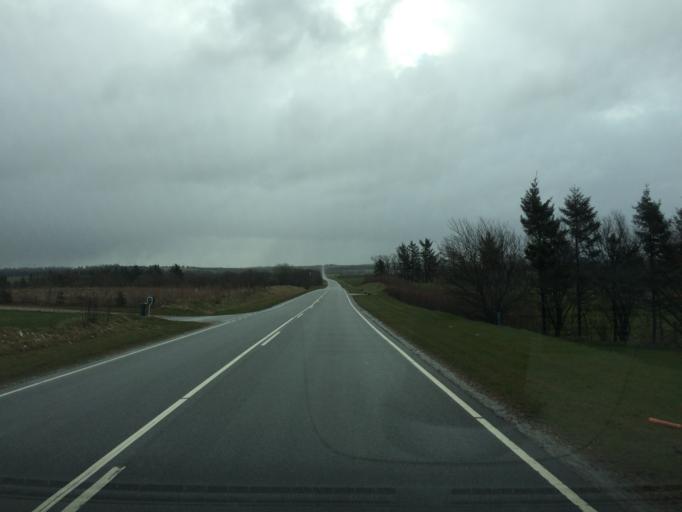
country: DK
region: Central Jutland
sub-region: Ringkobing-Skjern Kommune
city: Videbaek
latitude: 56.1919
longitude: 8.5800
